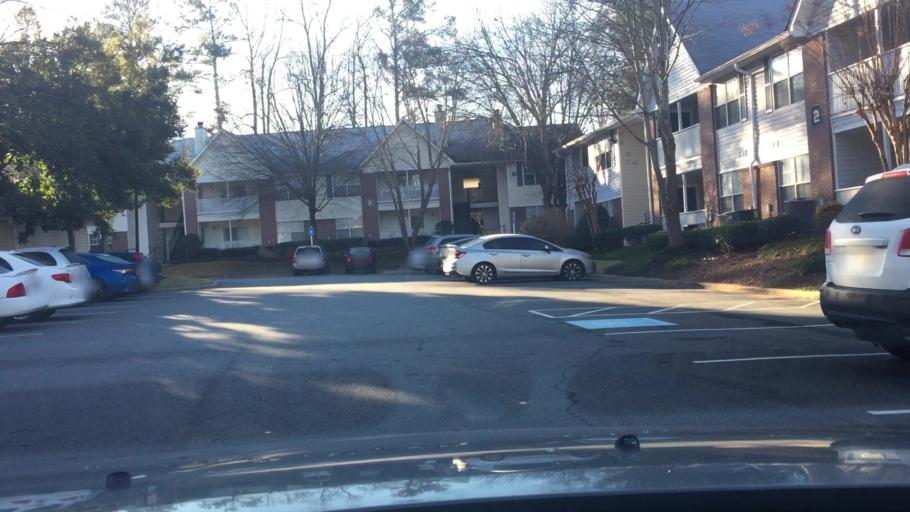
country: US
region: Georgia
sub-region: Cobb County
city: Kennesaw
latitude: 34.0461
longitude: -84.6237
